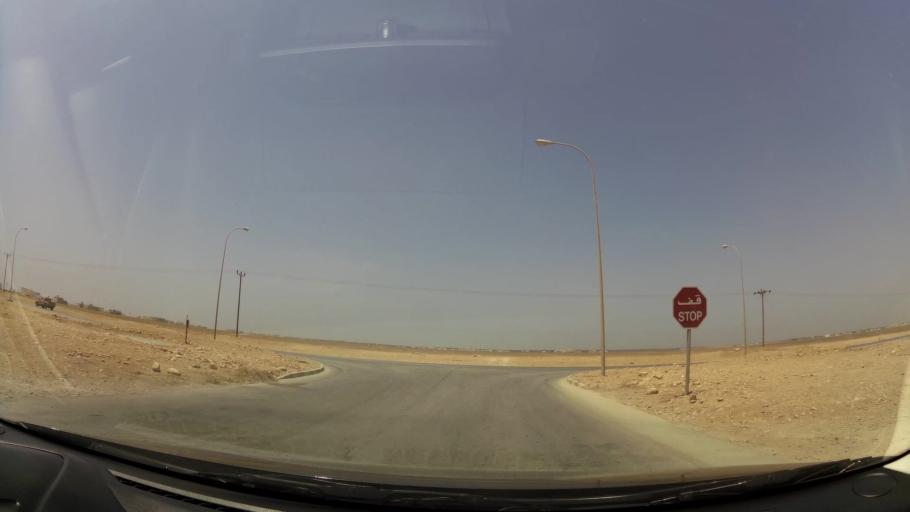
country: OM
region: Zufar
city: Salalah
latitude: 17.0688
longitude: 54.2055
